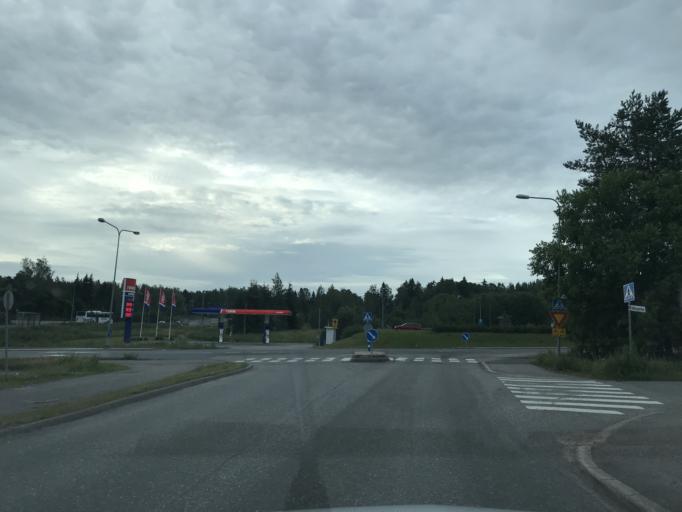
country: FI
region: Uusimaa
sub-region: Helsinki
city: Nurmijaervi
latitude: 60.3738
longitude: 24.7594
